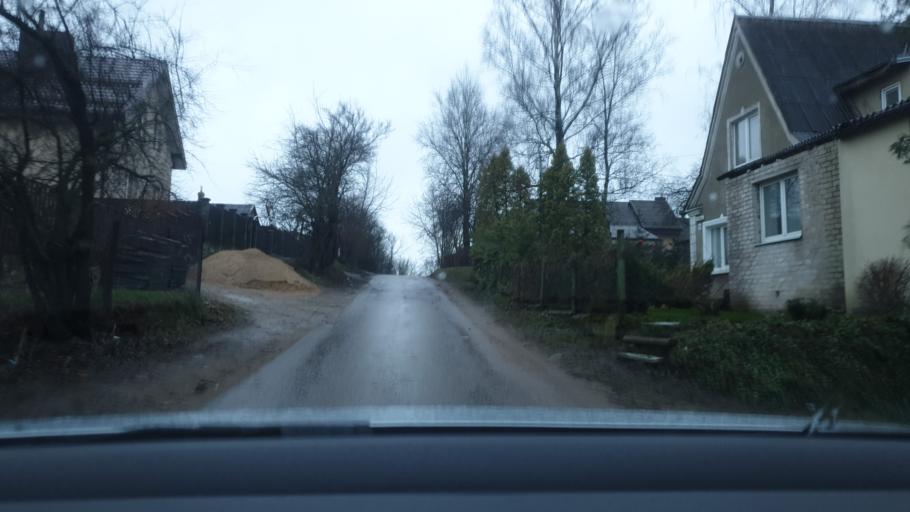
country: LT
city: Skaidiskes
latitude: 54.7030
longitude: 25.4093
